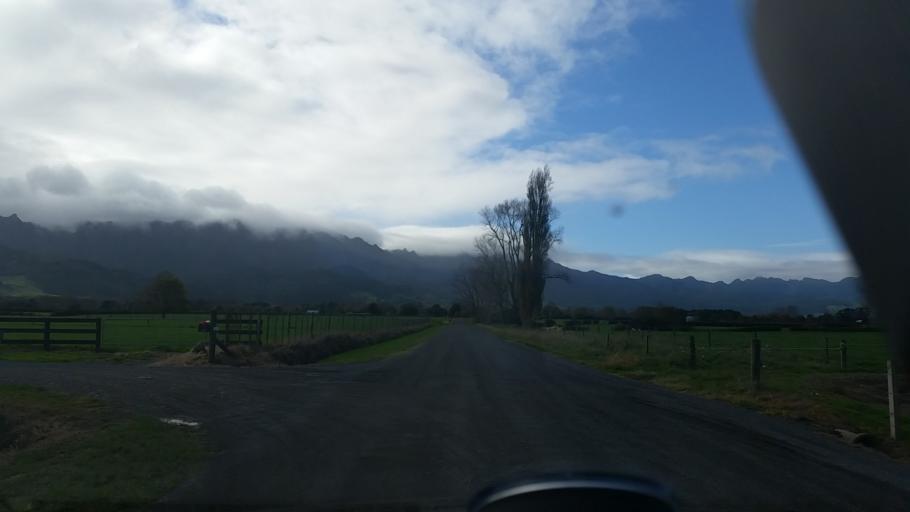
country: NZ
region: Bay of Plenty
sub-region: Western Bay of Plenty District
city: Katikati
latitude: -37.5775
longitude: 175.7249
